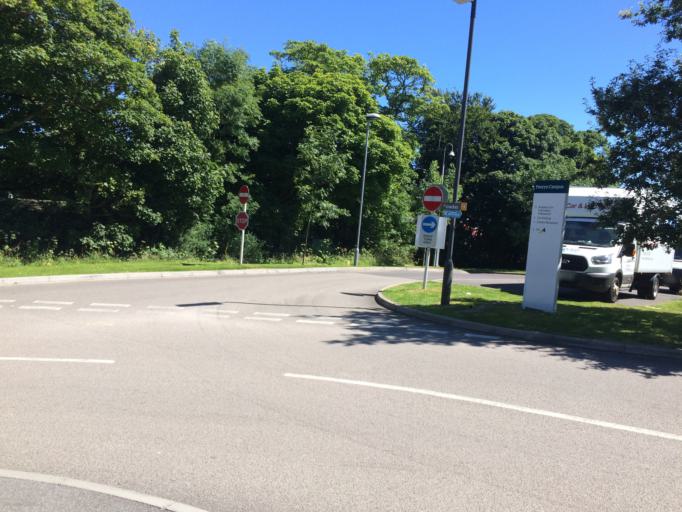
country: GB
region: England
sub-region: Cornwall
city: Penryn
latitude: 50.1718
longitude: -5.1241
